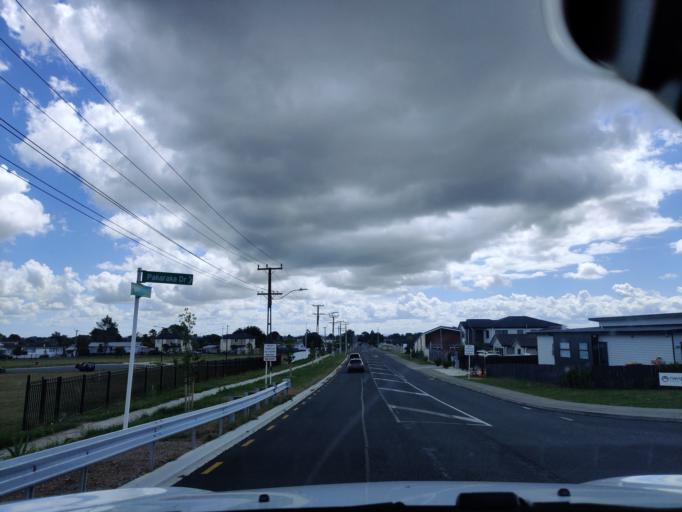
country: NZ
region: Auckland
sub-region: Auckland
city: Red Hill
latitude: -37.0533
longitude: 174.9680
